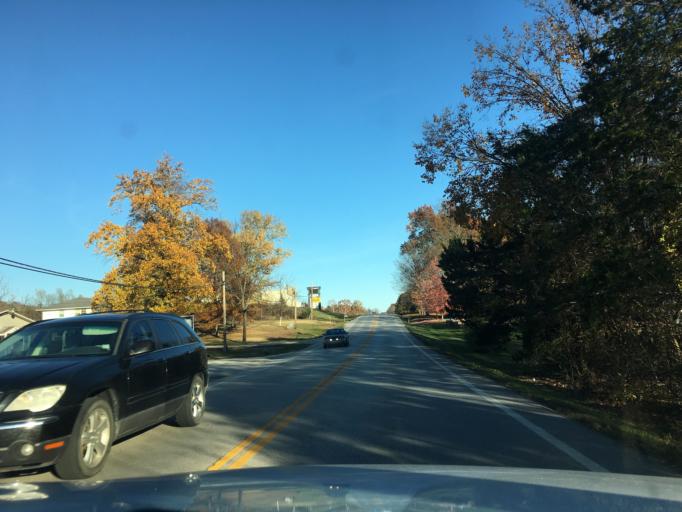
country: US
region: Missouri
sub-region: Franklin County
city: New Haven
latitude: 38.6003
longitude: -91.2372
